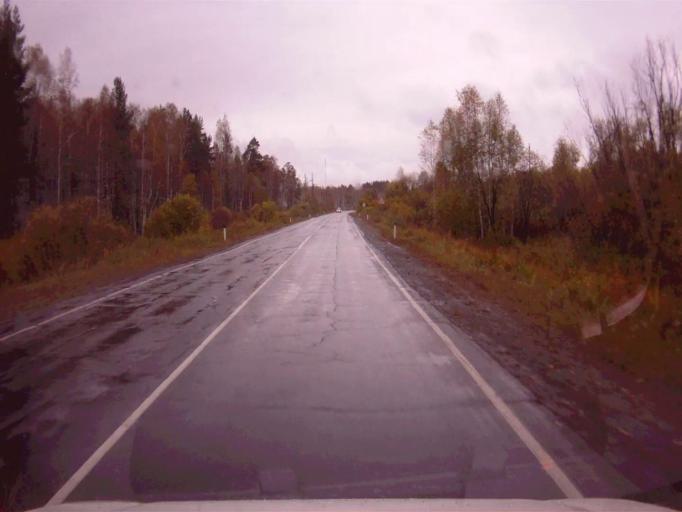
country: RU
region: Chelyabinsk
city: Verkhniy Ufaley
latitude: 55.9902
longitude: 60.3342
